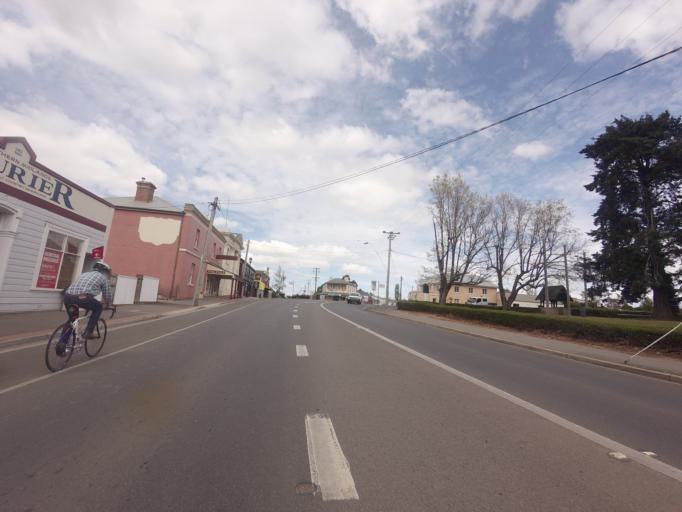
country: AU
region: Tasmania
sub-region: Northern Midlands
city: Longford
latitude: -41.5942
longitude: 147.1221
